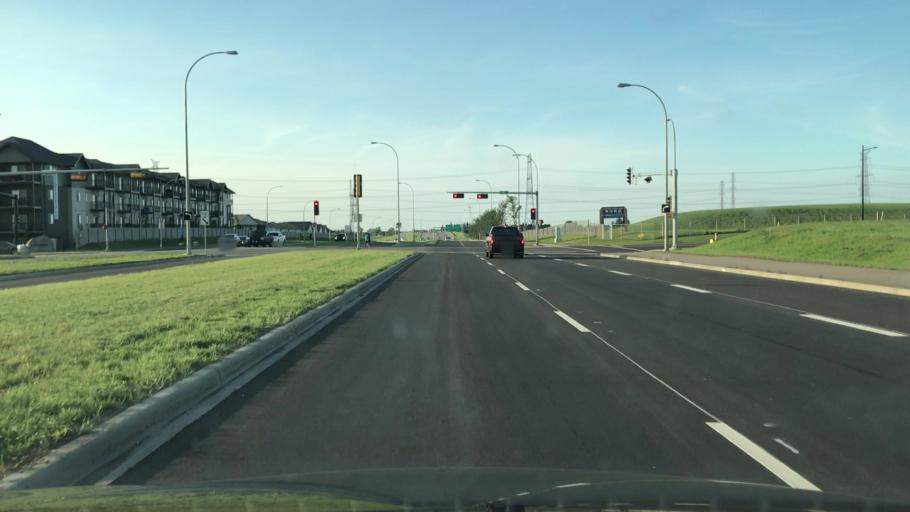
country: CA
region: Alberta
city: Beaumont
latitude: 53.4278
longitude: -113.4178
